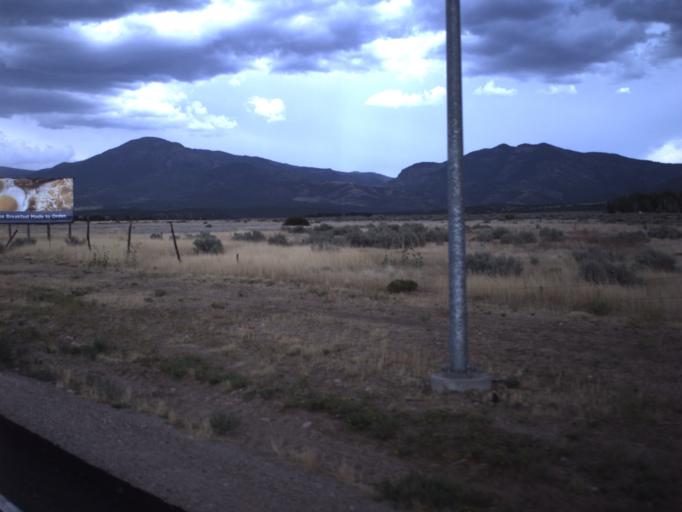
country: US
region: Utah
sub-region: Millard County
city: Fillmore
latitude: 38.9509
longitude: -112.3434
